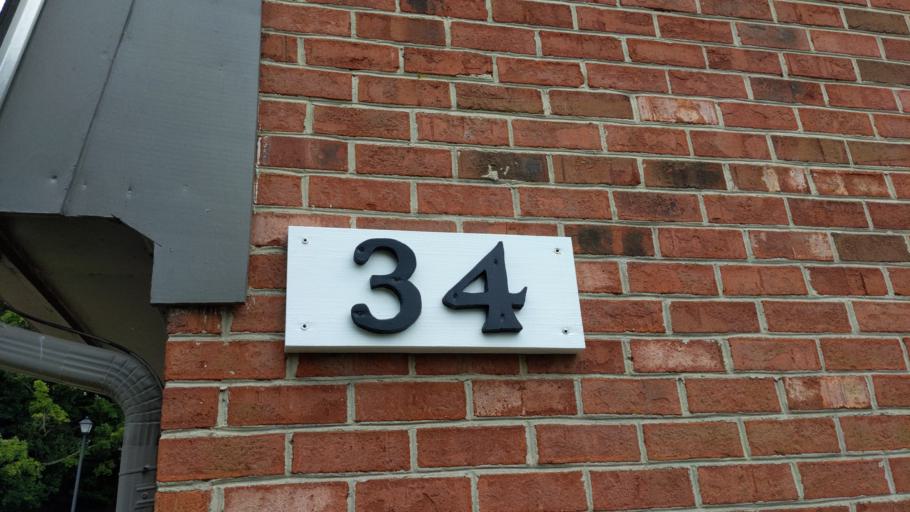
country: US
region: Virginia
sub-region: Montgomery County
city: Blacksburg
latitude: 37.2423
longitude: -80.4262
